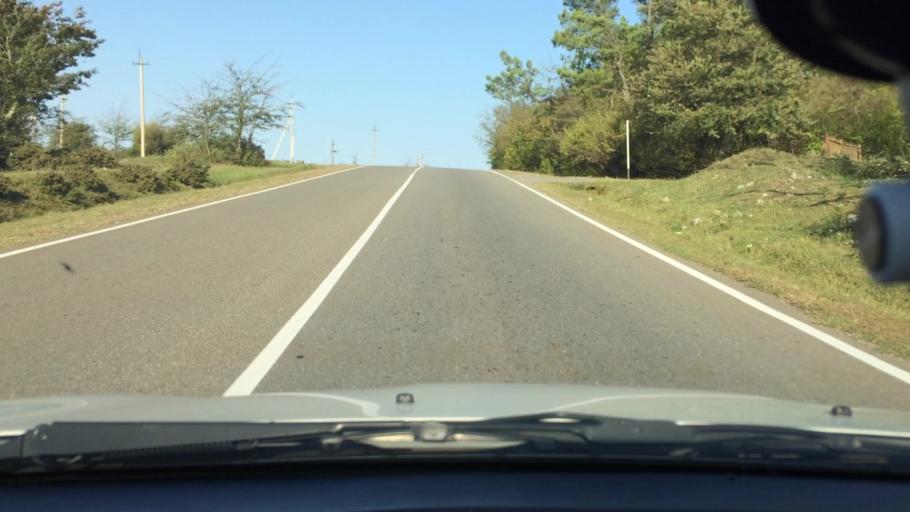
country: GE
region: Imereti
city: Kutaisi
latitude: 42.2514
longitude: 42.7517
